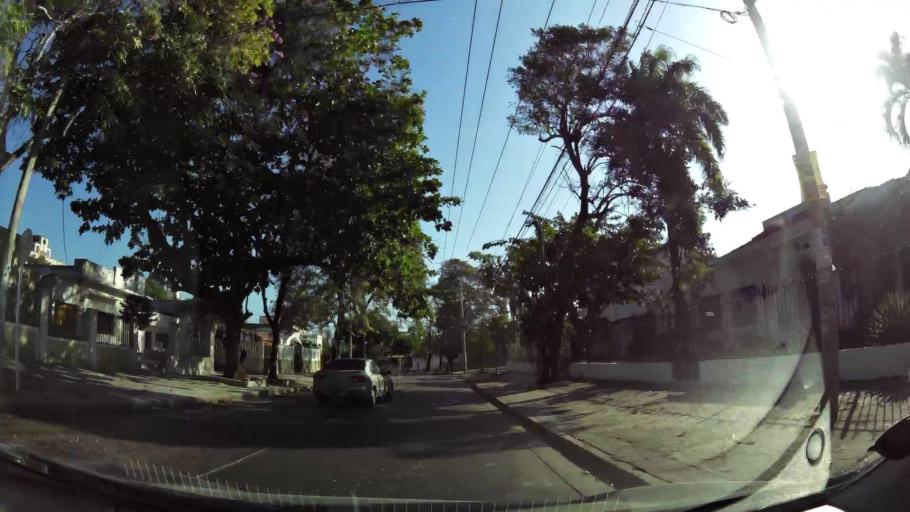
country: CO
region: Atlantico
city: Barranquilla
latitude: 10.9966
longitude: -74.7936
